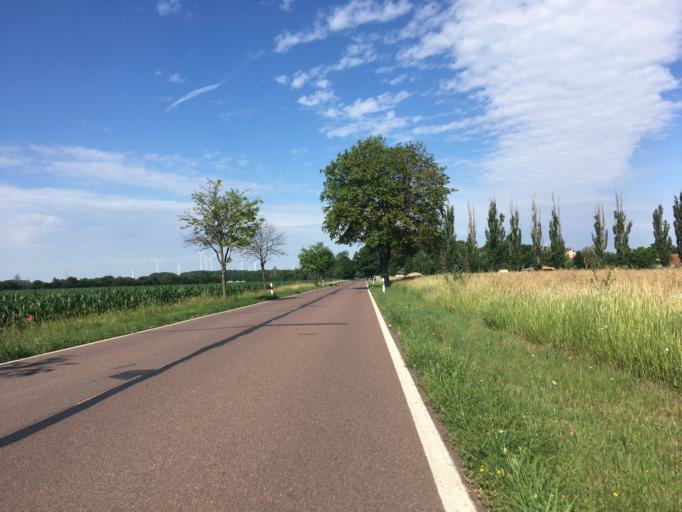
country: DE
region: Saxony-Anhalt
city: Wulfen
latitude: 51.7714
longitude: 11.8863
